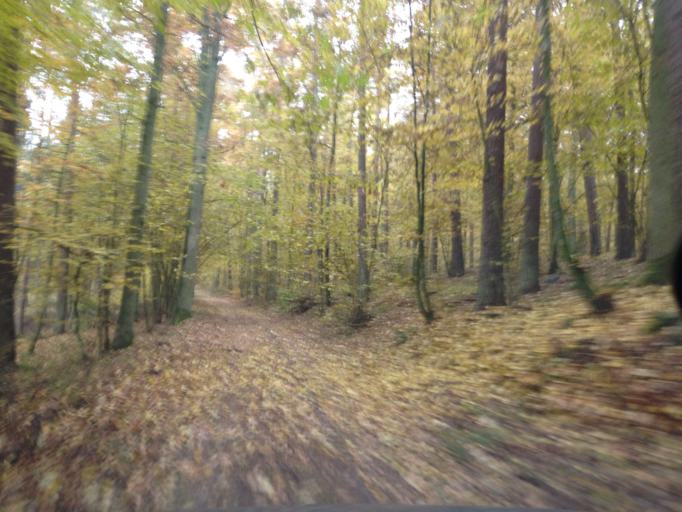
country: PL
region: Kujawsko-Pomorskie
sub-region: Powiat brodnicki
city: Gorzno
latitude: 53.2258
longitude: 19.7150
